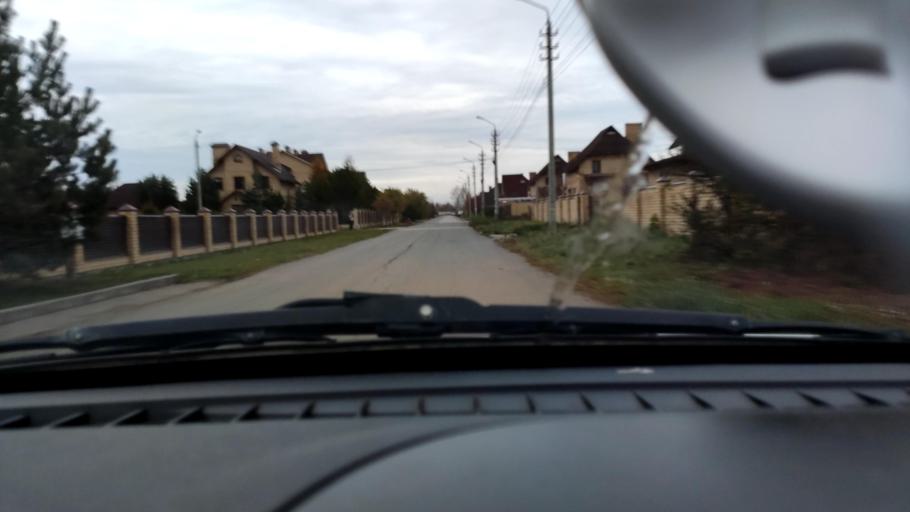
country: RU
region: Perm
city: Kondratovo
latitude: 57.9736
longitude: 56.1142
